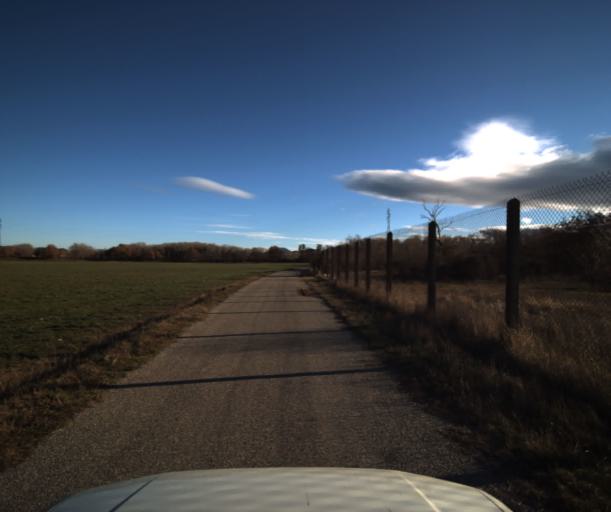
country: FR
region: Provence-Alpes-Cote d'Azur
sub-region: Departement des Bouches-du-Rhone
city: Le Puy-Sainte-Reparade
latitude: 43.6781
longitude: 5.4641
